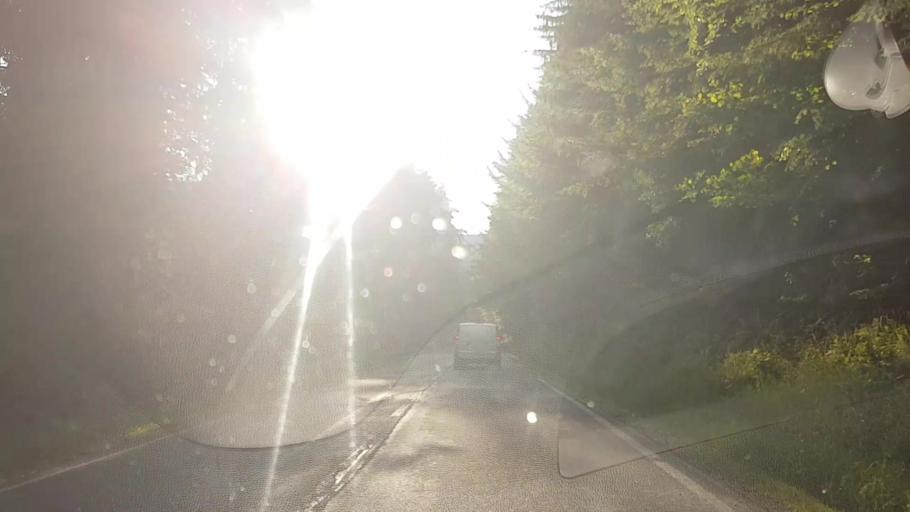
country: RO
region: Harghita
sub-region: Comuna Remetea
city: Remetea
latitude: 46.6730
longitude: 25.3441
